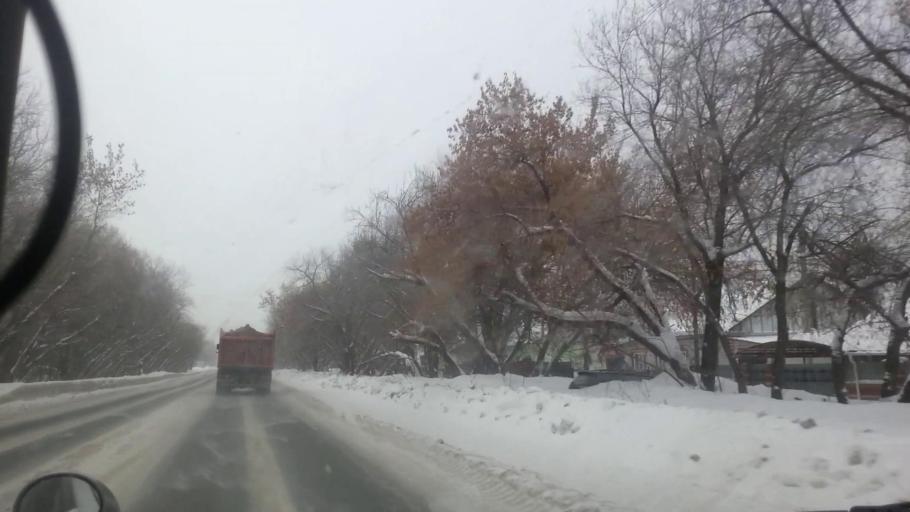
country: RU
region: Altai Krai
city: Vlasikha
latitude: 53.3007
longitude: 83.5964
